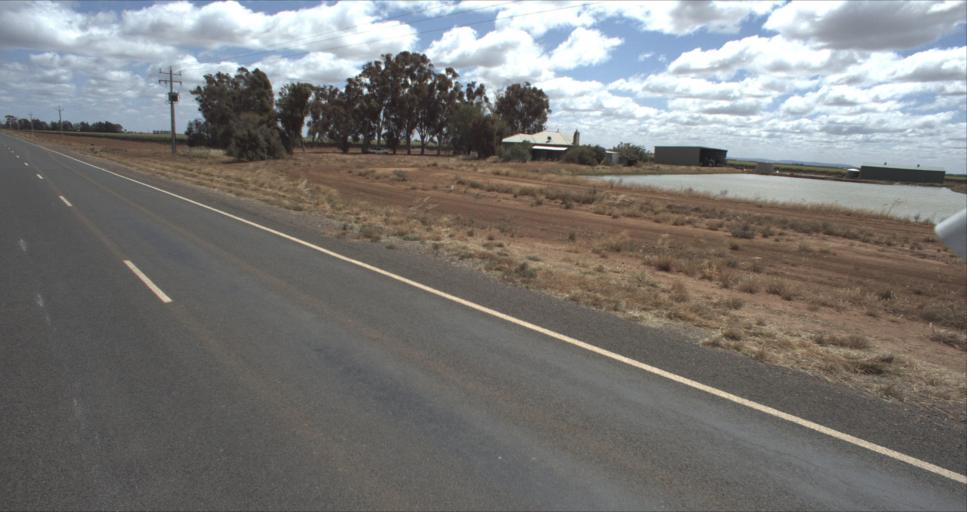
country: AU
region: New South Wales
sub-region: Murrumbidgee Shire
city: Darlington Point
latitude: -34.4735
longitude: 146.1452
